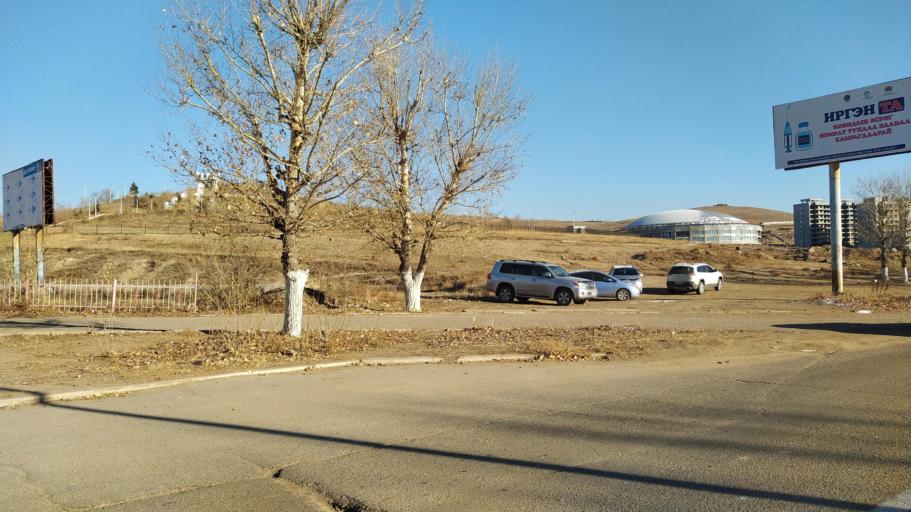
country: MN
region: Orhon
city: Erdenet
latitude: 49.0323
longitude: 104.0611
